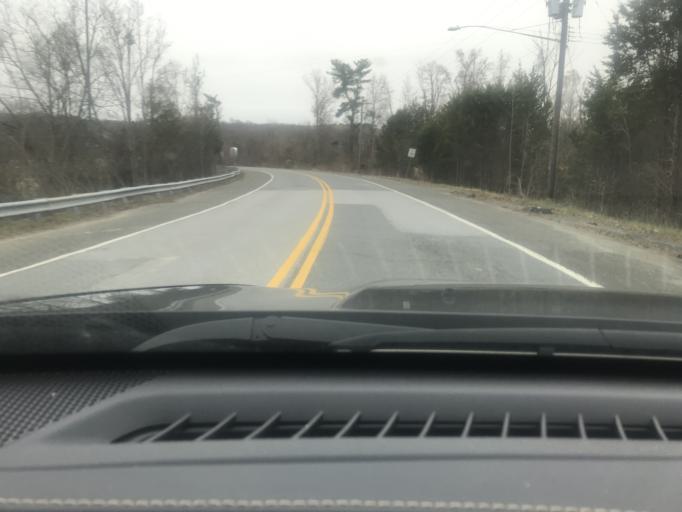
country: US
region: Maryland
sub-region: Prince George's County
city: Oxon Hill
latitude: 38.7867
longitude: -76.9789
